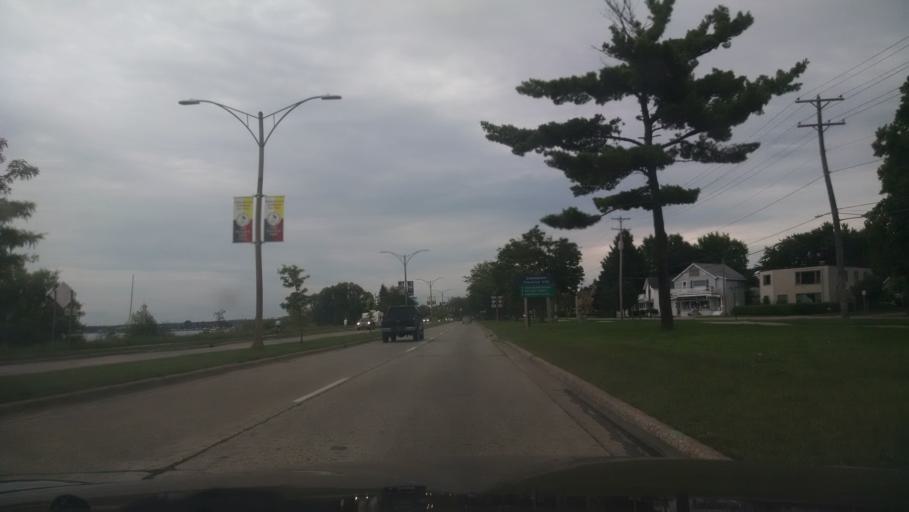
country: US
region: Michigan
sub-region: Leelanau County
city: Greilickville
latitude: 44.7713
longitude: -85.6382
